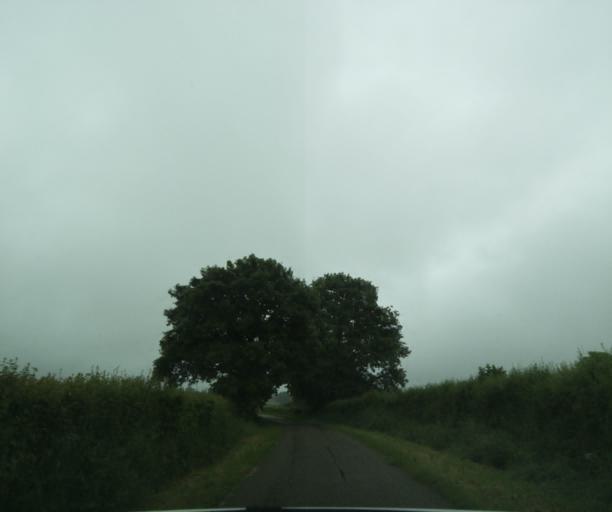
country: FR
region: Bourgogne
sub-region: Departement de Saone-et-Loire
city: Charolles
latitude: 46.4608
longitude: 4.2304
